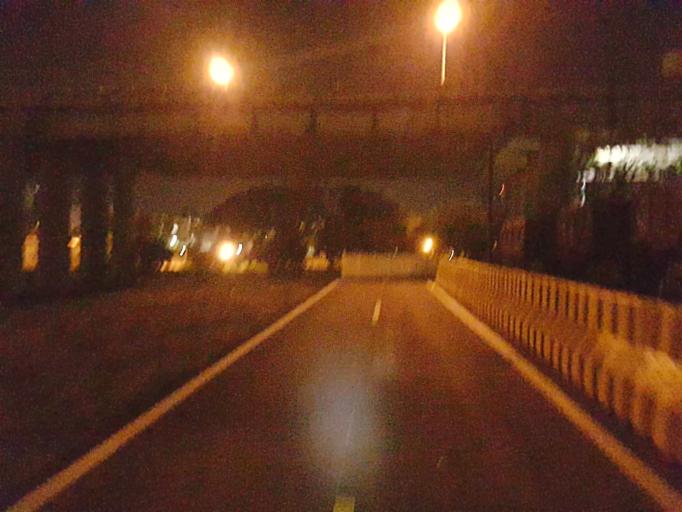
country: TW
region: Taipei
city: Taipei
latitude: 24.9948
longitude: 121.5347
